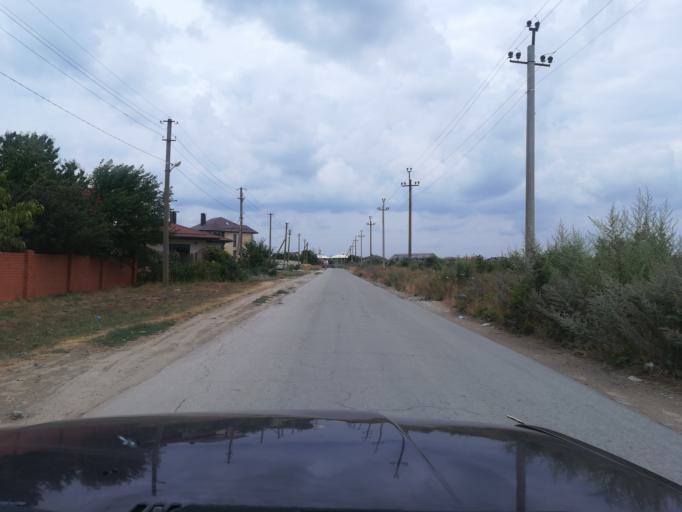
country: RU
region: Krasnodarskiy
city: Vityazevo
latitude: 45.0139
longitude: 37.2948
